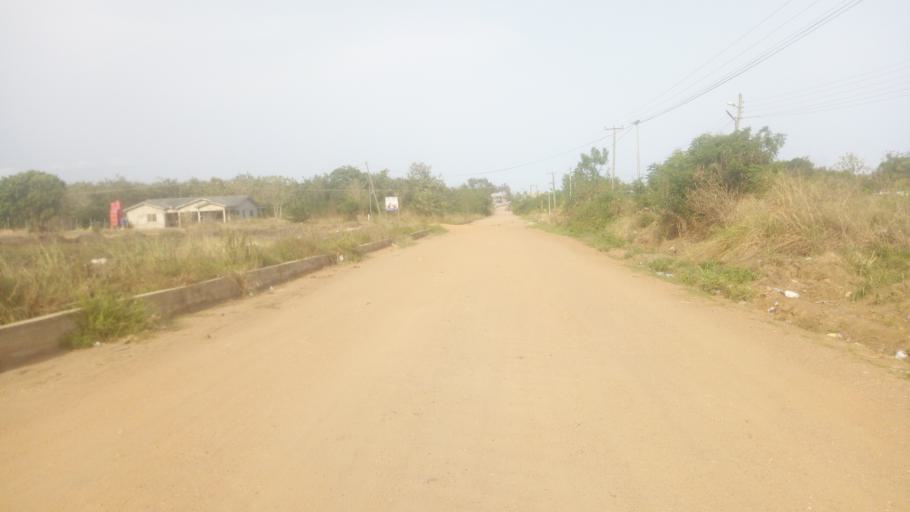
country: GH
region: Central
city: Winneba
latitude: 5.3763
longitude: -0.6384
